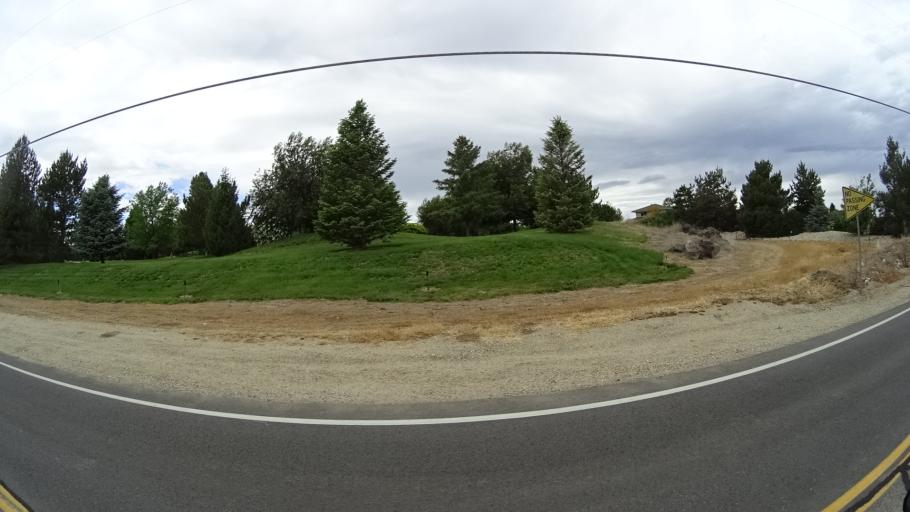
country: US
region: Idaho
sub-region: Ada County
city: Meridian
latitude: 43.5807
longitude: -116.4137
